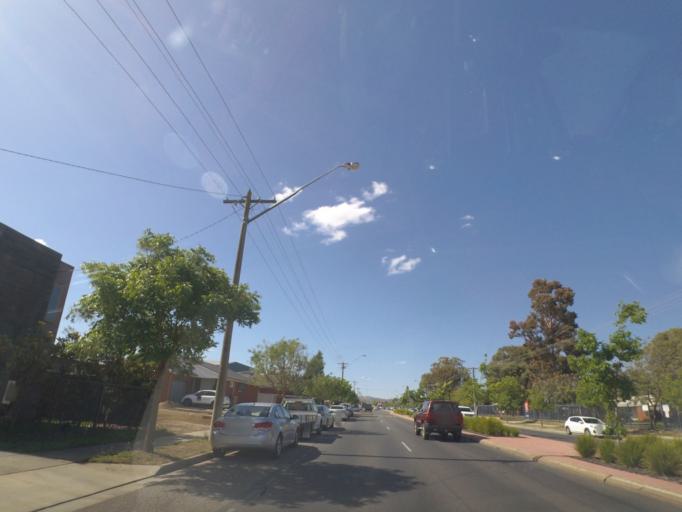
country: AU
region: New South Wales
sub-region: Albury Municipality
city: North Albury
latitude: -36.0649
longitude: 146.9311
